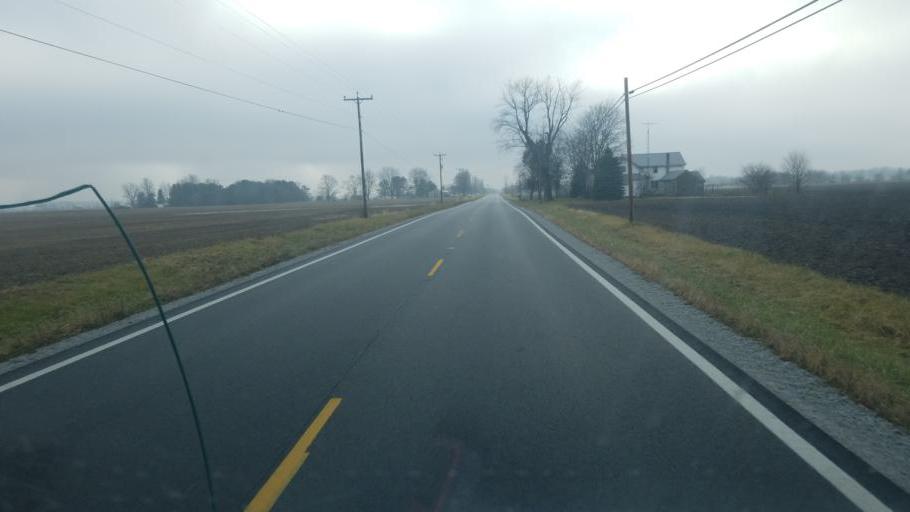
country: US
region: Ohio
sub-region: Hardin County
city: Kenton
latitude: 40.6771
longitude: -83.5219
